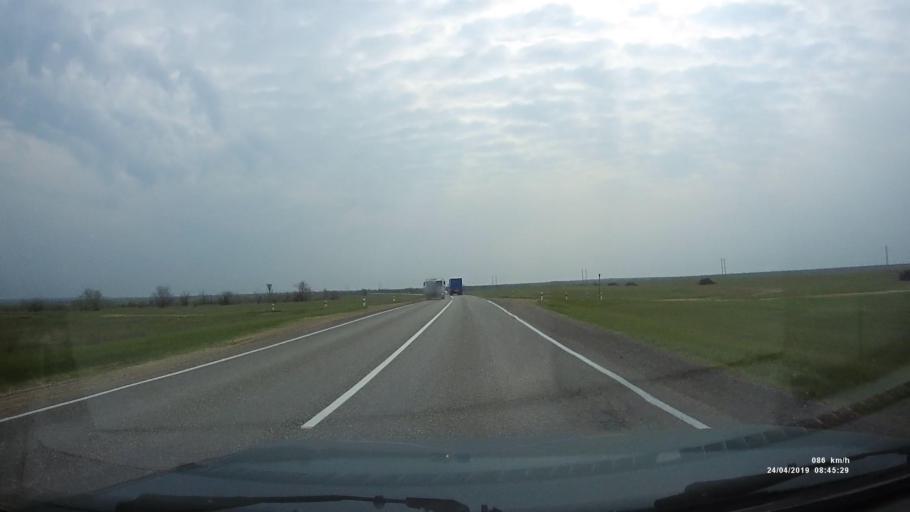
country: RU
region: Kalmykiya
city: Arshan'
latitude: 46.2360
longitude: 44.0615
